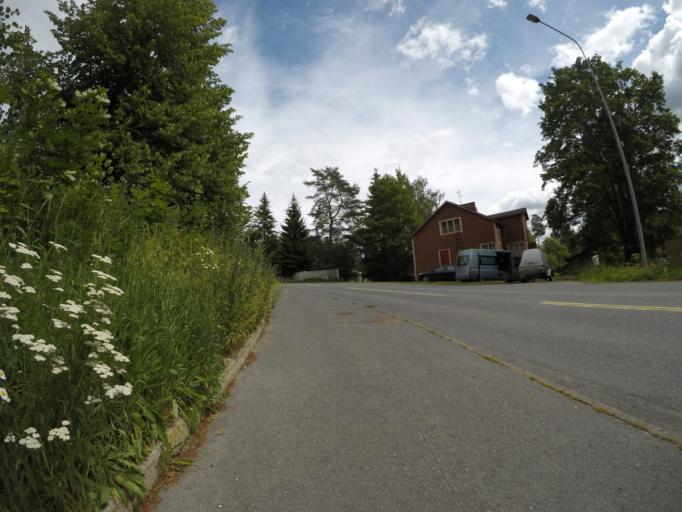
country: FI
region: Haeme
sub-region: Haemeenlinna
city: Haemeenlinna
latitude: 60.9714
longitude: 24.4281
